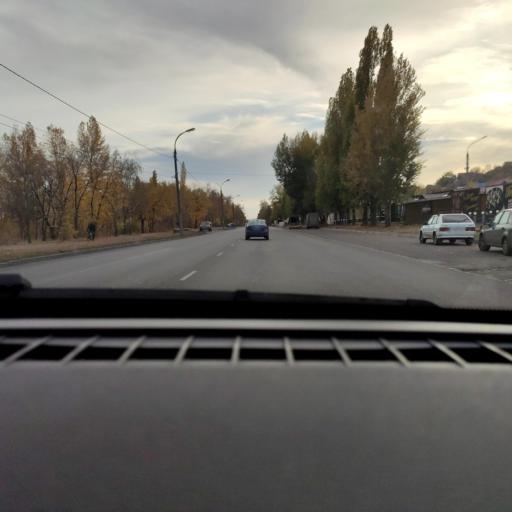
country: RU
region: Voronezj
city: Voronezh
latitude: 51.6478
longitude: 39.2113
